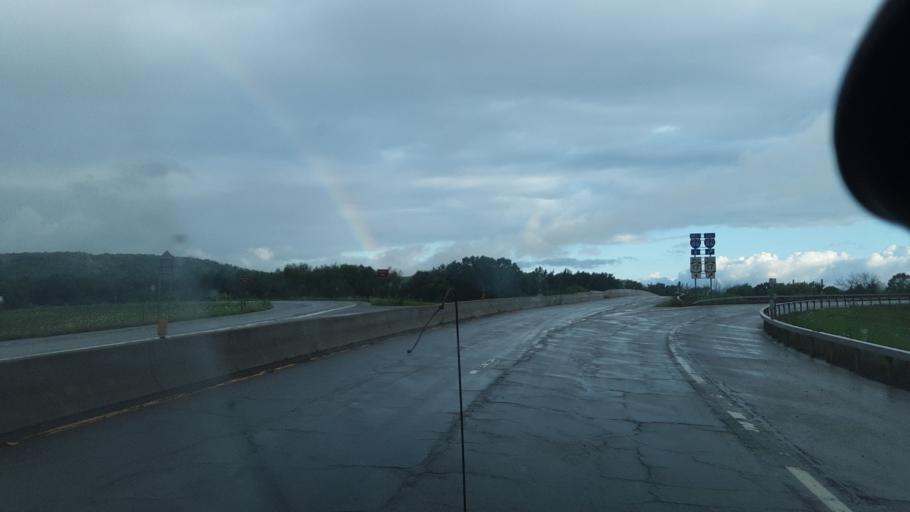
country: US
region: New York
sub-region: Chautauqua County
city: Falconer
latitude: 42.1281
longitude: -79.1893
